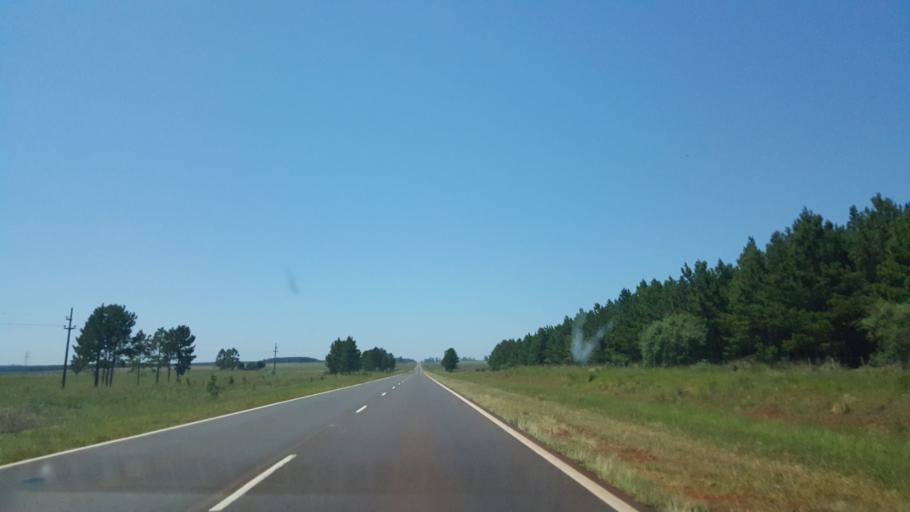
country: AR
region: Corrientes
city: Santo Tome
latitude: -28.3918
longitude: -56.1076
